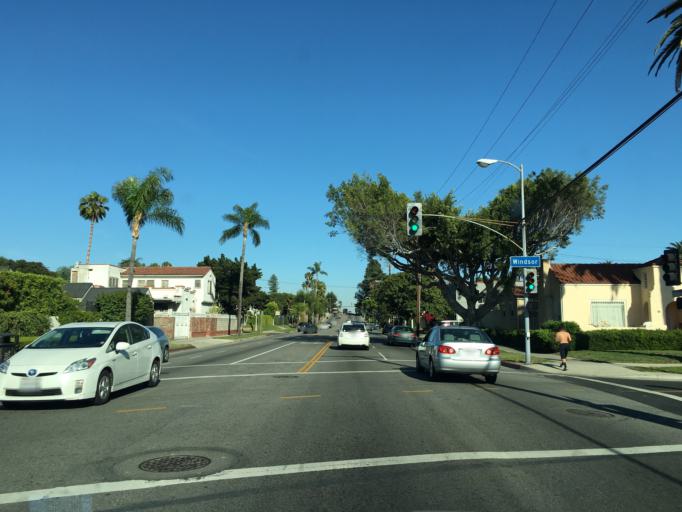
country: US
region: California
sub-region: Los Angeles County
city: Hollywood
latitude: 34.0762
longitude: -118.3197
